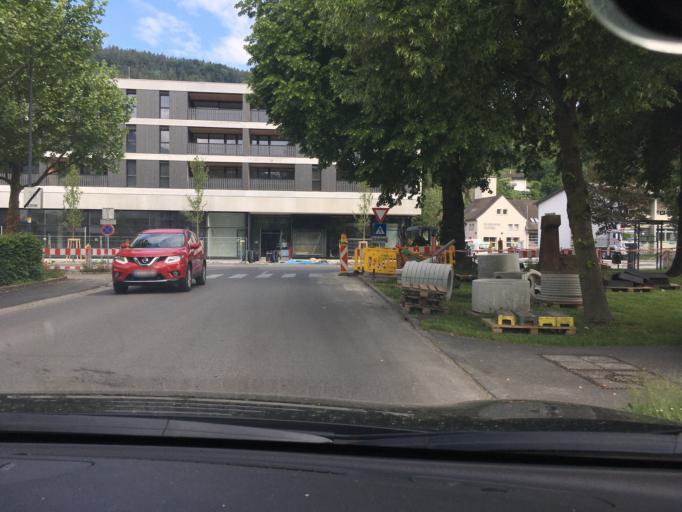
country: AT
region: Vorarlberg
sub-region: Politischer Bezirk Feldkirch
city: Nofels
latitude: 47.2379
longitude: 9.5768
